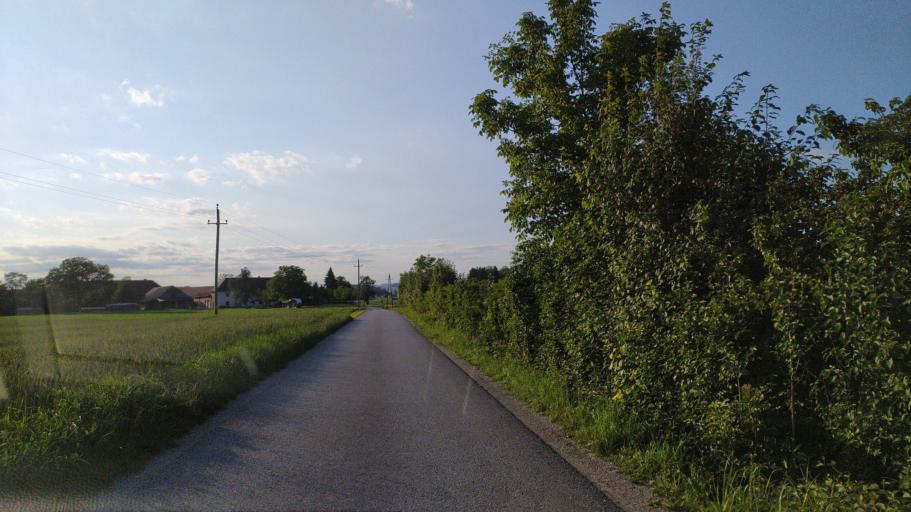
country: AT
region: Lower Austria
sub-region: Politischer Bezirk Amstetten
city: Ennsdorf
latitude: 48.2217
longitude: 14.5661
